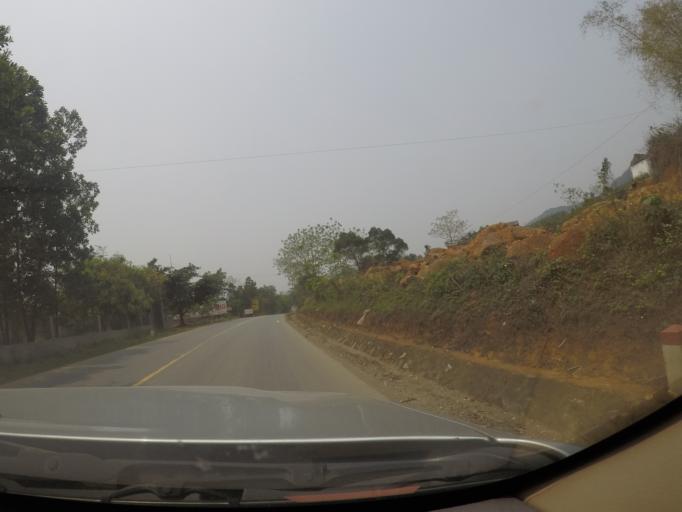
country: VN
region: Thanh Hoa
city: Thi Tran Cam Thuy
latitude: 20.1424
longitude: 105.4300
